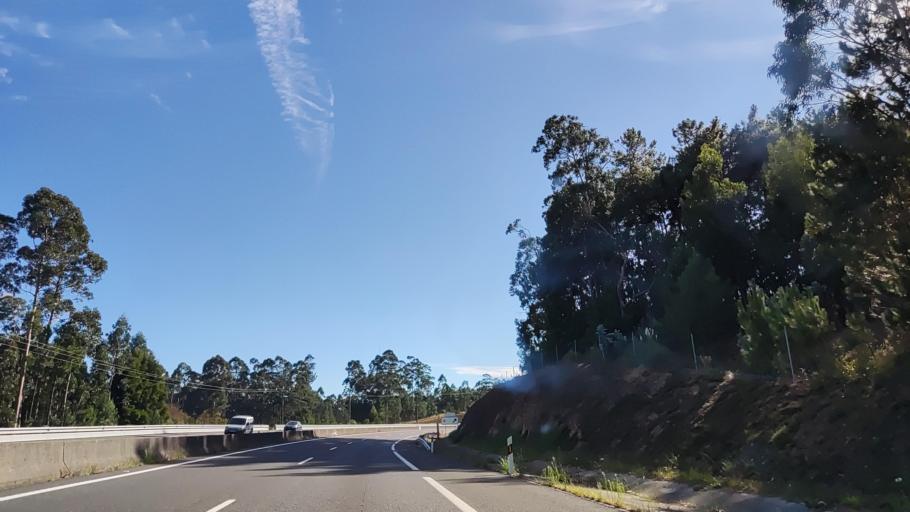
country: ES
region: Galicia
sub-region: Provincia da Coruna
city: Boiro
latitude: 42.6155
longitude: -8.9539
